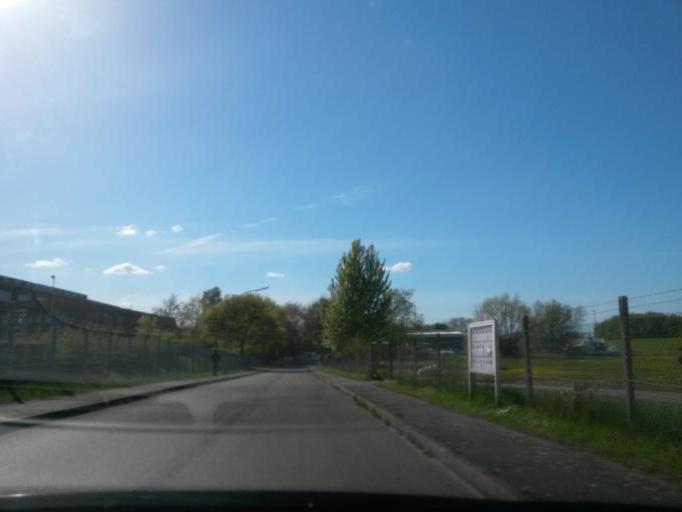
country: DE
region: Schleswig-Holstein
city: Wedel
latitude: 53.5730
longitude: 9.6890
